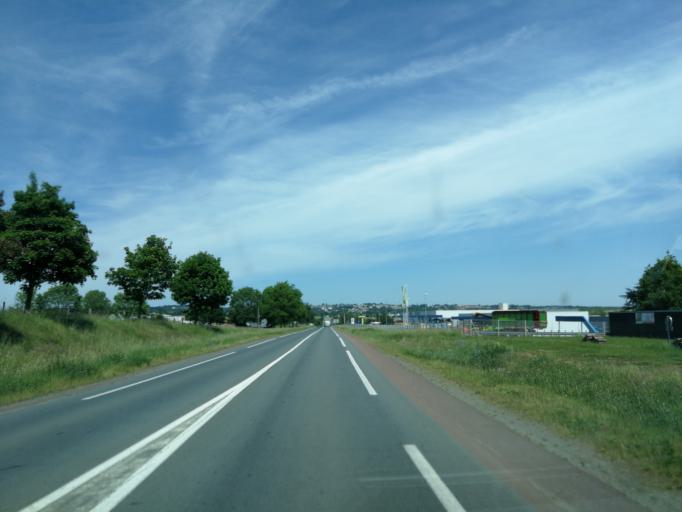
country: FR
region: Pays de la Loire
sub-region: Departement de la Vendee
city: Antigny
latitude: 46.6228
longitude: -0.7768
